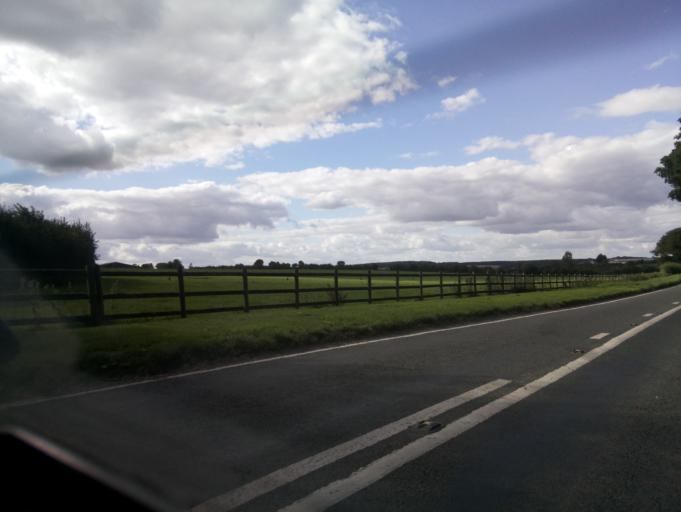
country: GB
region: England
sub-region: Hampshire
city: Winchester
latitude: 51.0885
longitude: -1.3771
